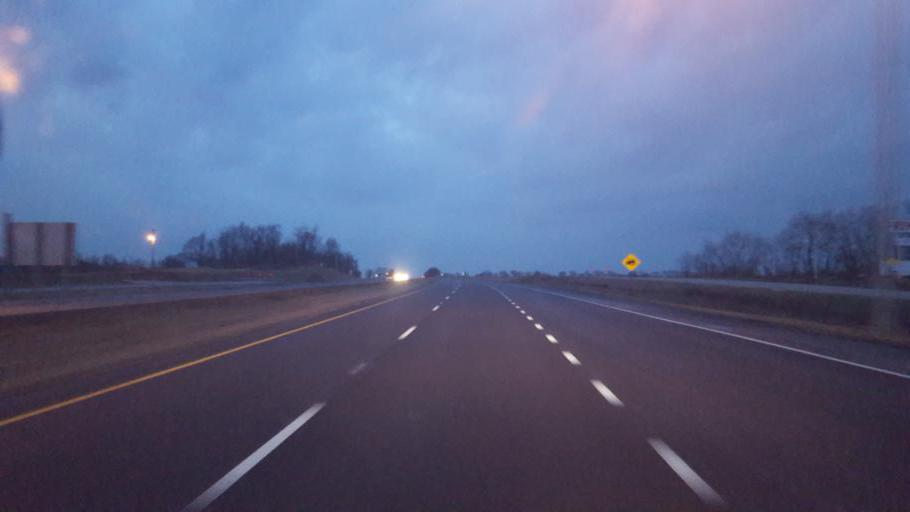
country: US
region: Ohio
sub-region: Ross County
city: Kingston
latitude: 39.4200
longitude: -82.9748
